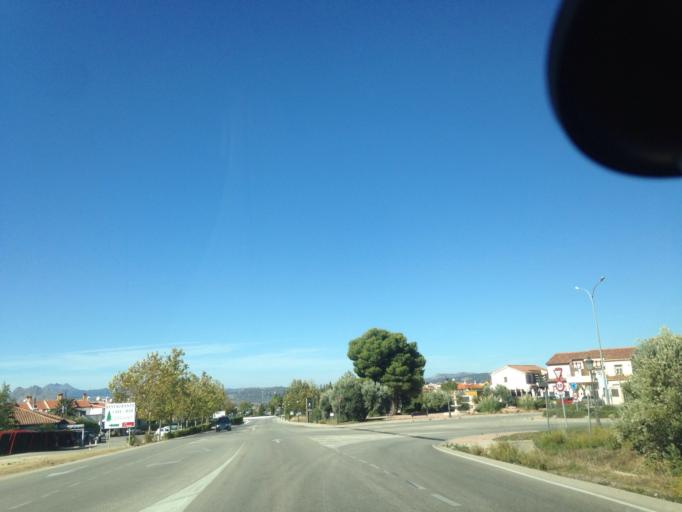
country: ES
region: Andalusia
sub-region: Provincia de Malaga
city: Ronda
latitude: 36.7264
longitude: -5.1493
